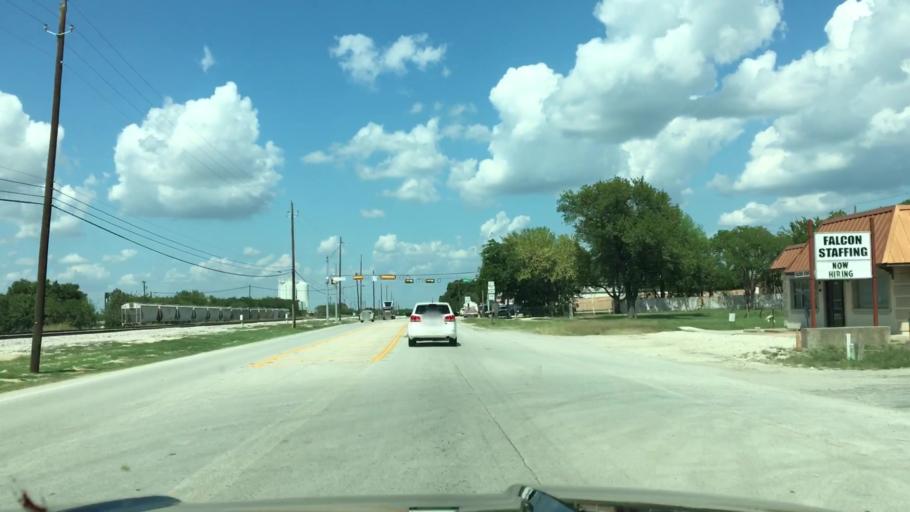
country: US
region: Texas
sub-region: Denton County
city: Roanoke
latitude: 32.9981
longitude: -97.2310
